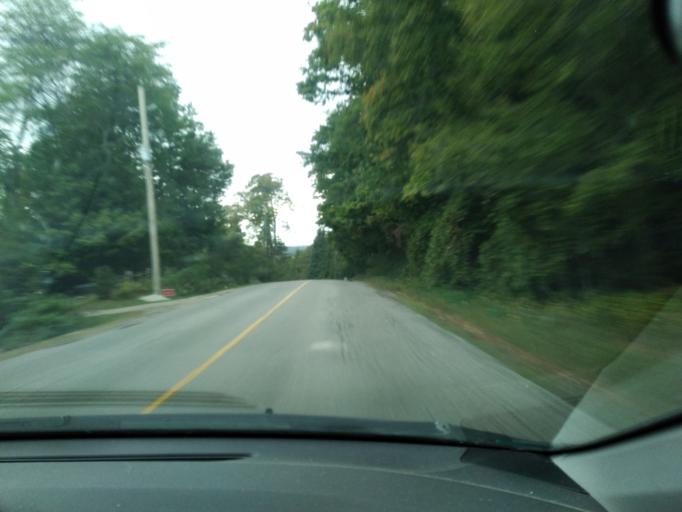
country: CA
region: Ontario
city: Bradford West Gwillimbury
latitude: 43.9533
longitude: -79.7772
